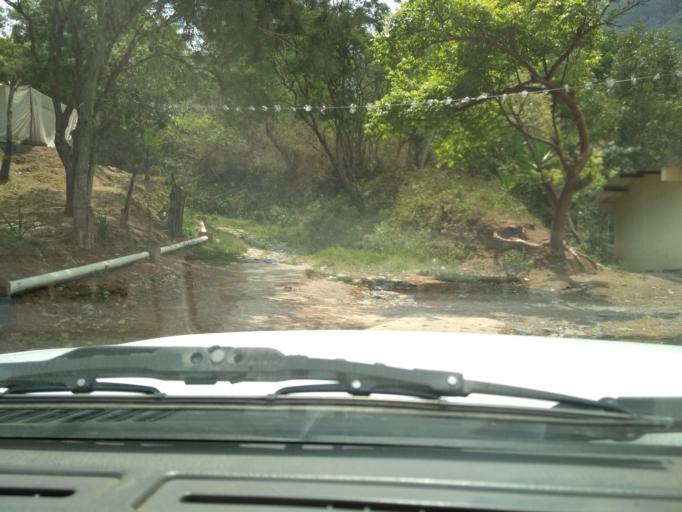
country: MX
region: Veracruz
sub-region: Camerino Z. Mendoza
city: La Cuesta
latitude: 18.7934
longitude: -97.1760
